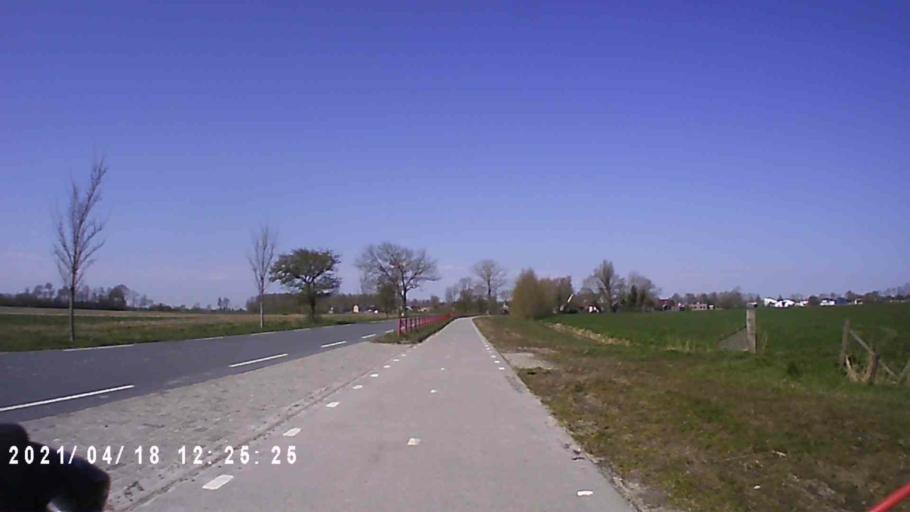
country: NL
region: Friesland
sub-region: Gemeente Dongeradeel
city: Anjum
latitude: 53.3282
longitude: 6.1113
